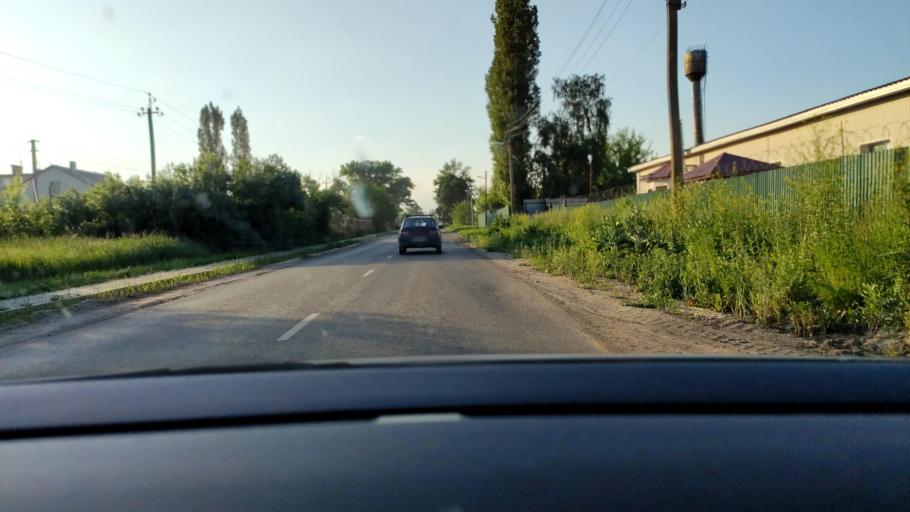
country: RU
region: Voronezj
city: Maslovka
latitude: 51.5377
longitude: 39.3425
